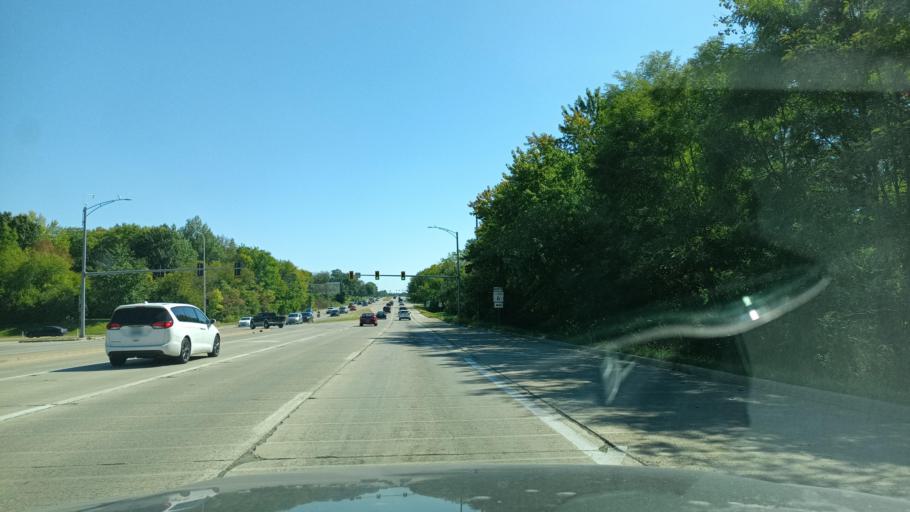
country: US
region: Illinois
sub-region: Peoria County
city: Dunlap
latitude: 40.7745
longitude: -89.6685
